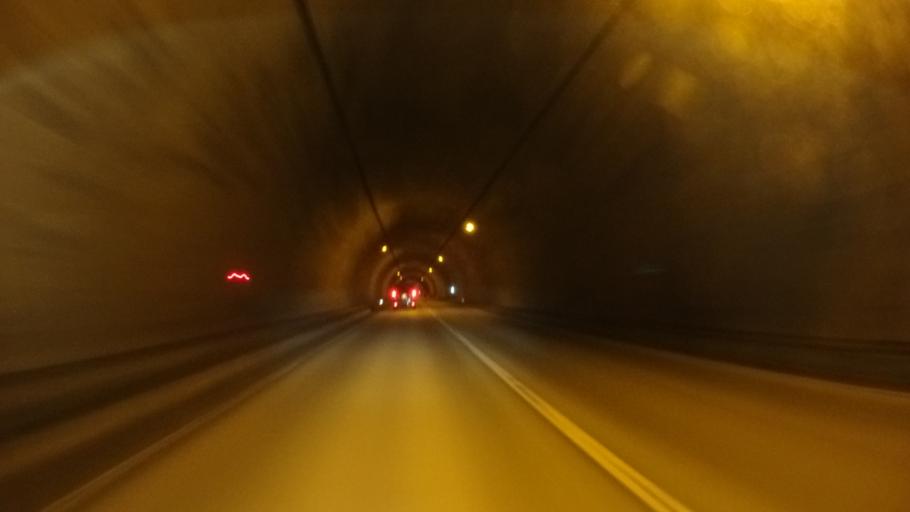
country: JP
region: Ishikawa
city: Nanao
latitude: 37.3297
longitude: 136.8206
